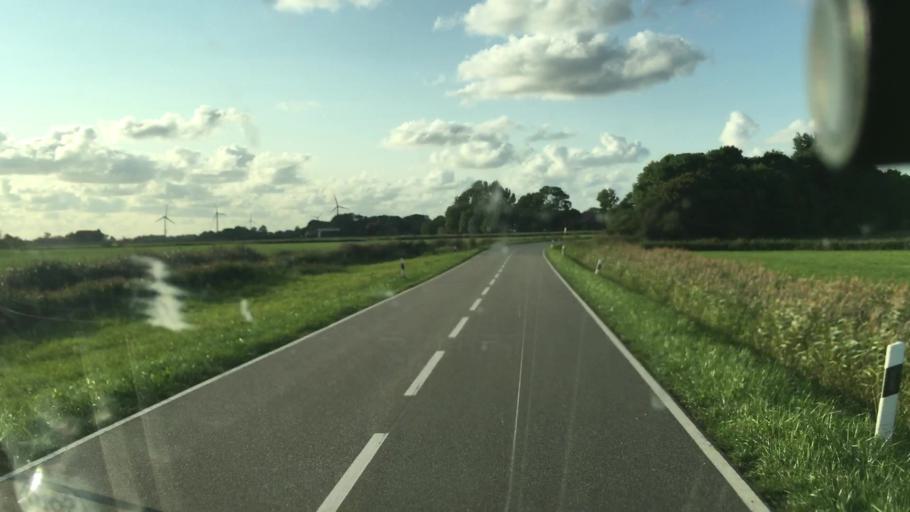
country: DE
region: Lower Saxony
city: Wittmund
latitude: 53.6347
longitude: 7.8306
